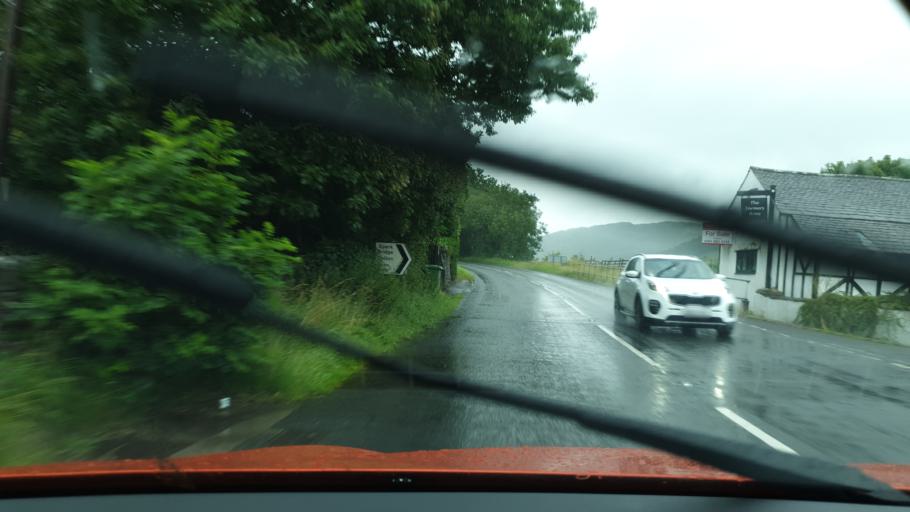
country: GB
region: England
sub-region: Cumbria
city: Ulverston
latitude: 54.2547
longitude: -3.0728
